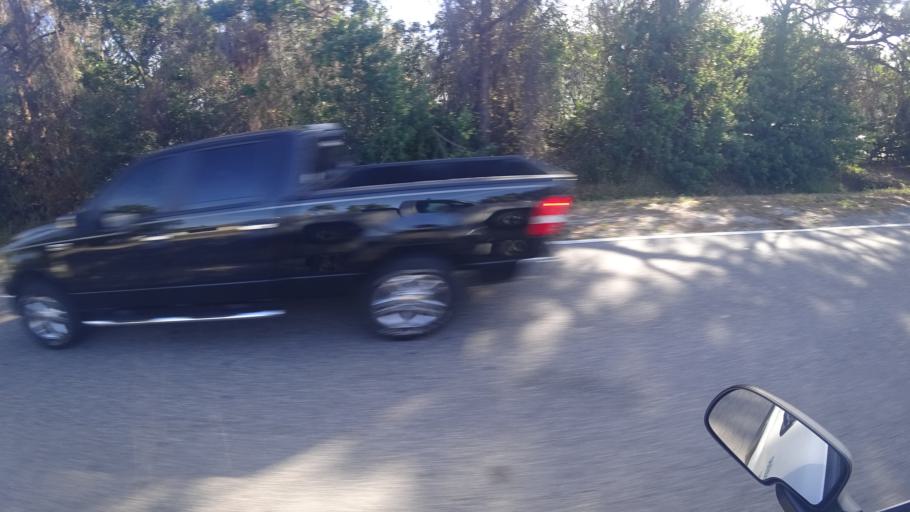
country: US
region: Florida
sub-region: Manatee County
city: South Bradenton
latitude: 27.4696
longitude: -82.6123
